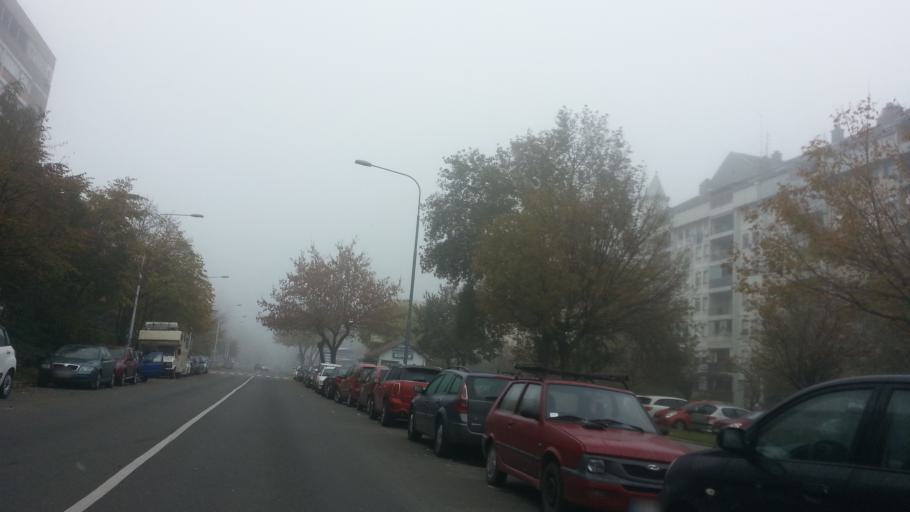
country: RS
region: Central Serbia
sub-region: Belgrade
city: Zemun
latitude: 44.8338
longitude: 20.4132
